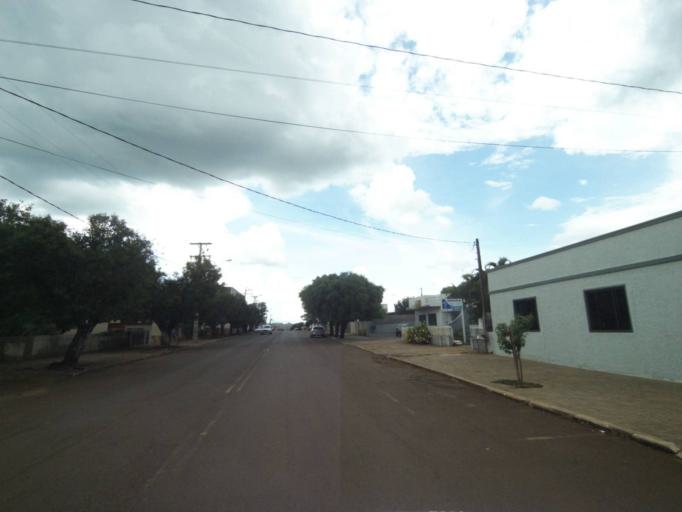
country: BR
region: Parana
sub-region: Guaraniacu
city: Guaraniacu
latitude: -25.0970
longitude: -52.8724
